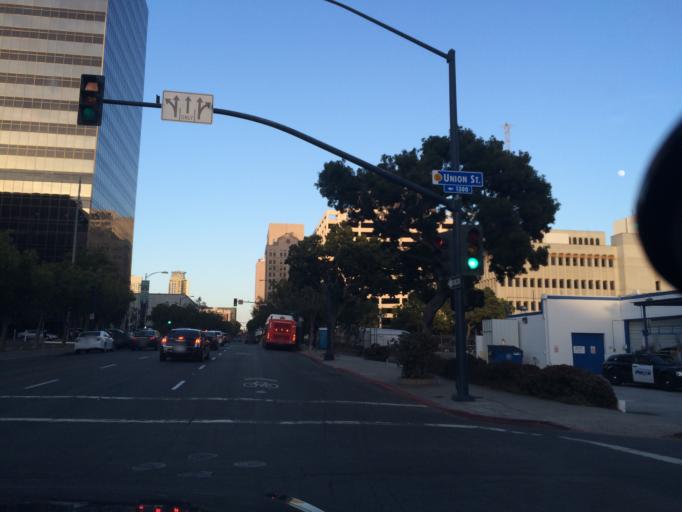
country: US
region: California
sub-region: San Diego County
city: San Diego
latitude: 32.7188
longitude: -117.1658
